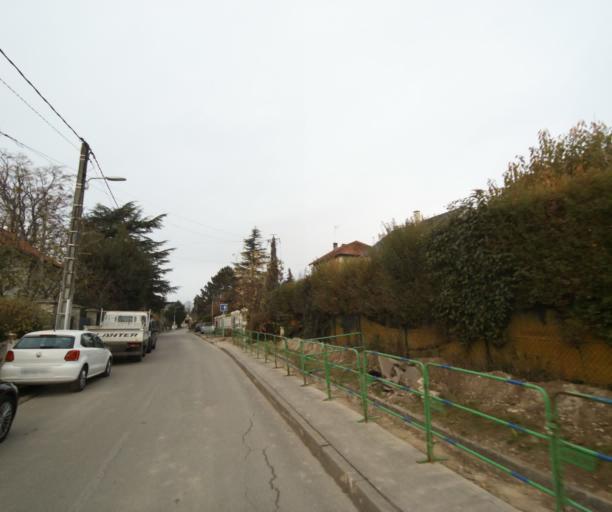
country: FR
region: Ile-de-France
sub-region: Departement des Yvelines
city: Triel-sur-Seine
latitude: 48.9879
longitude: 2.0000
